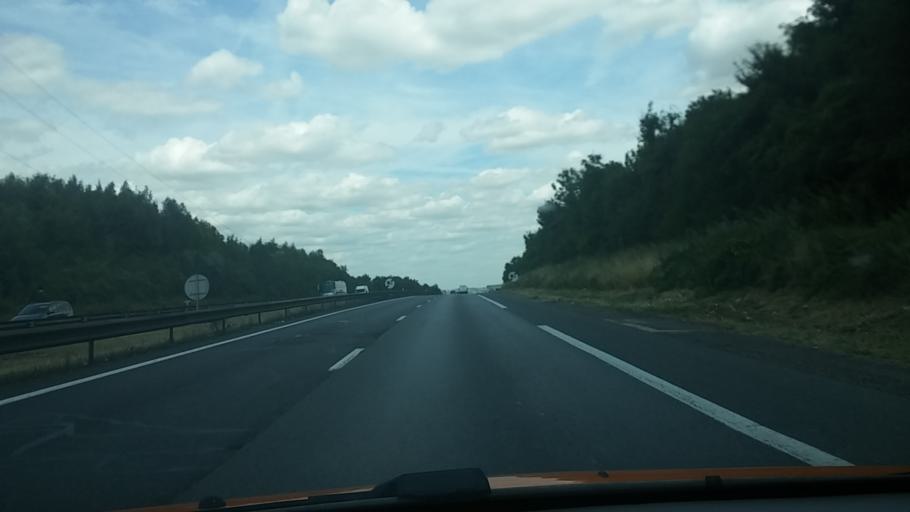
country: FR
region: Ile-de-France
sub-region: Departement de Seine-et-Marne
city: Le Pin
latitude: 48.9276
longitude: 2.6286
